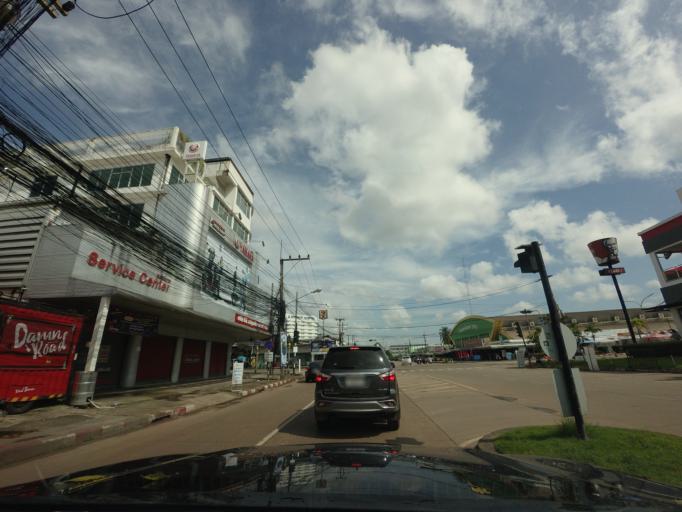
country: TH
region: Changwat Udon Thani
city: Udon Thani
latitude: 17.4036
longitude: 102.8040
